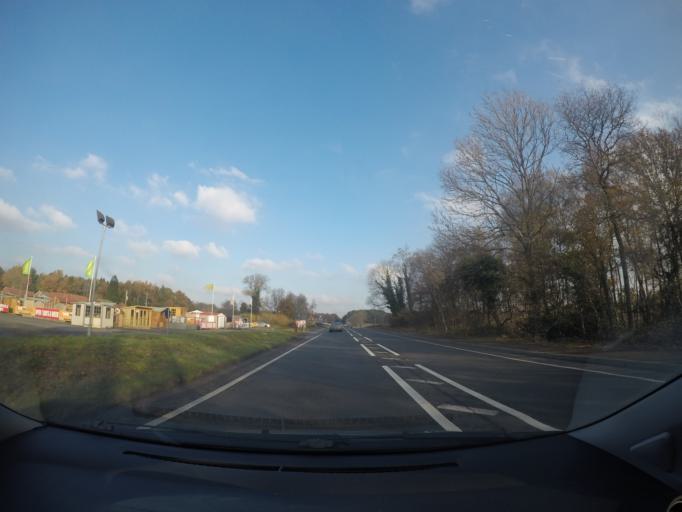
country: GB
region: England
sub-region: City of York
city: Holtby
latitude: 54.0153
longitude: -0.9845
